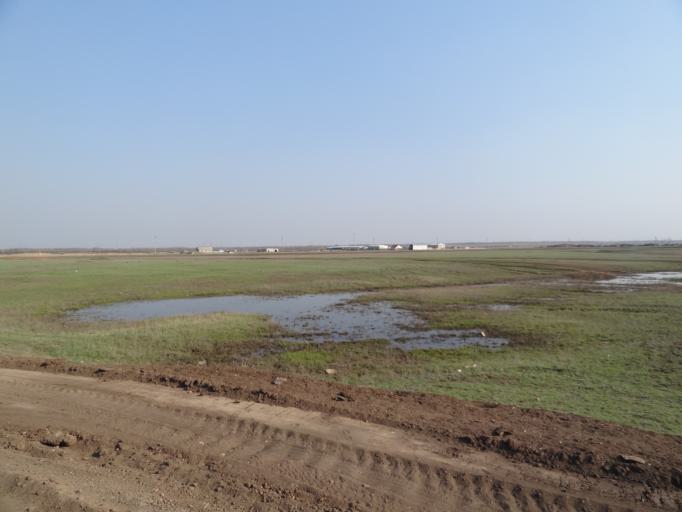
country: RU
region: Saratov
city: Privolzhskiy
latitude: 51.3235
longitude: 46.0068
